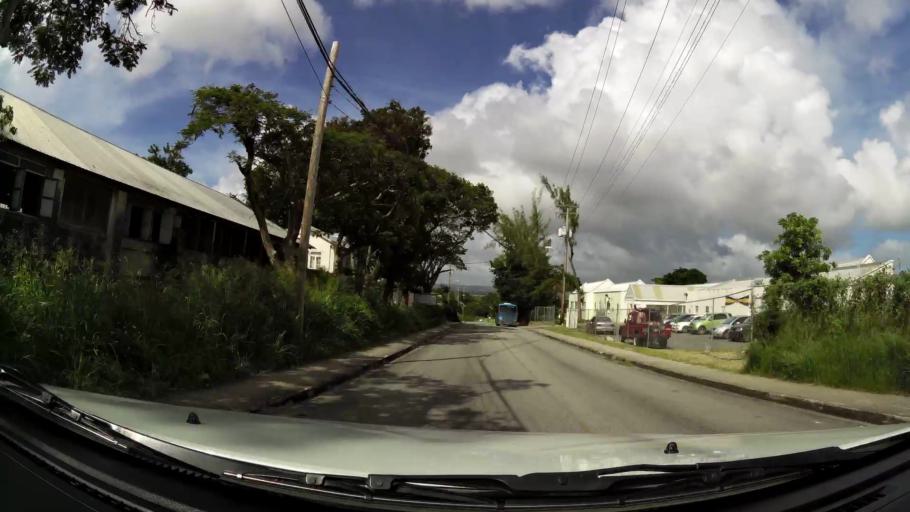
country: BB
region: Saint Michael
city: Bridgetown
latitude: 13.0945
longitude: -59.5934
